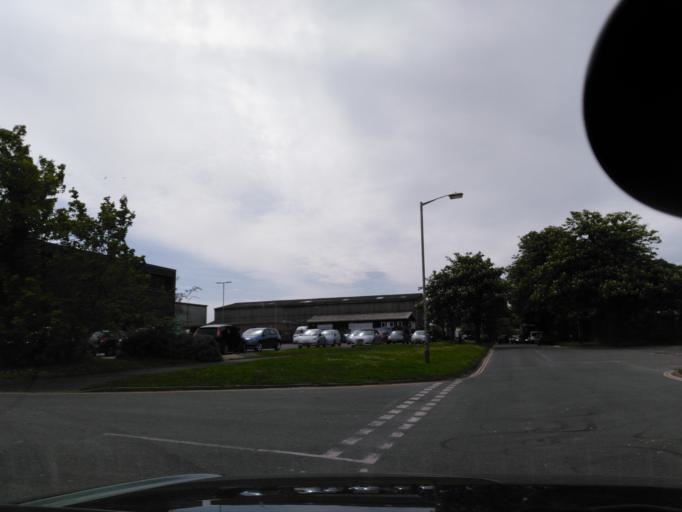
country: GB
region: England
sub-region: Wiltshire
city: Melksham
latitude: 51.3578
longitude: -2.1323
